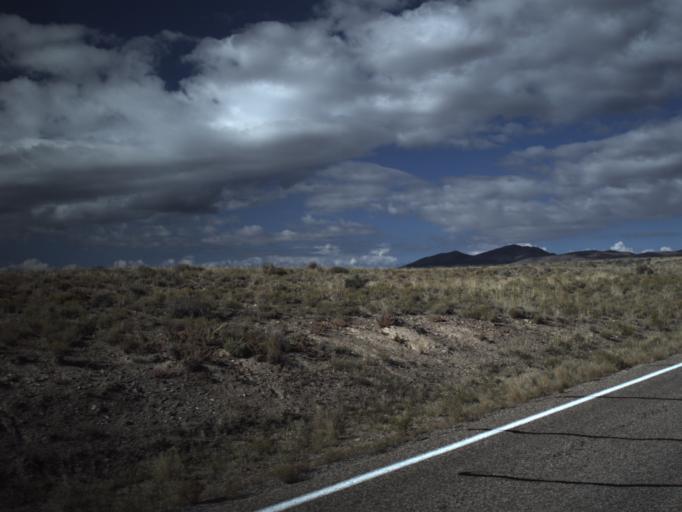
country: US
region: Utah
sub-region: Beaver County
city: Milford
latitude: 38.4411
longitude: -113.1648
